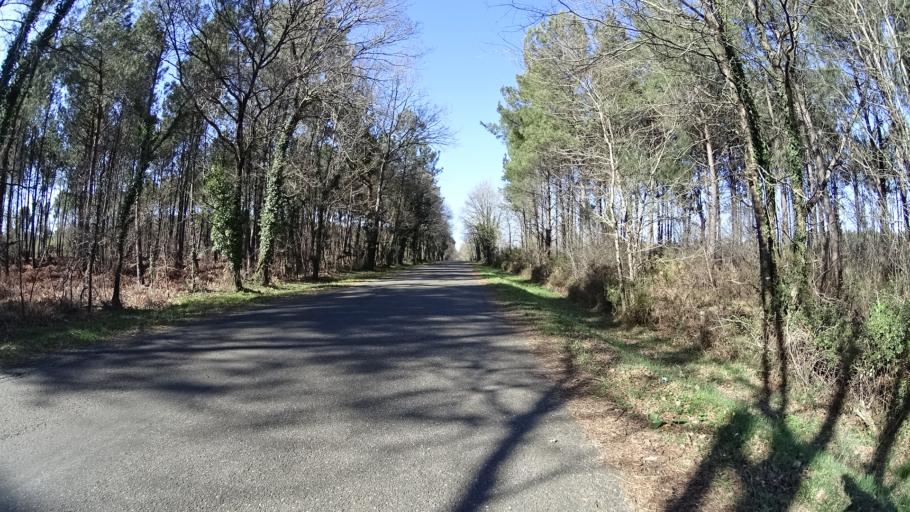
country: FR
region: Aquitaine
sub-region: Departement des Landes
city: Mees
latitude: 43.7313
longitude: -1.0938
